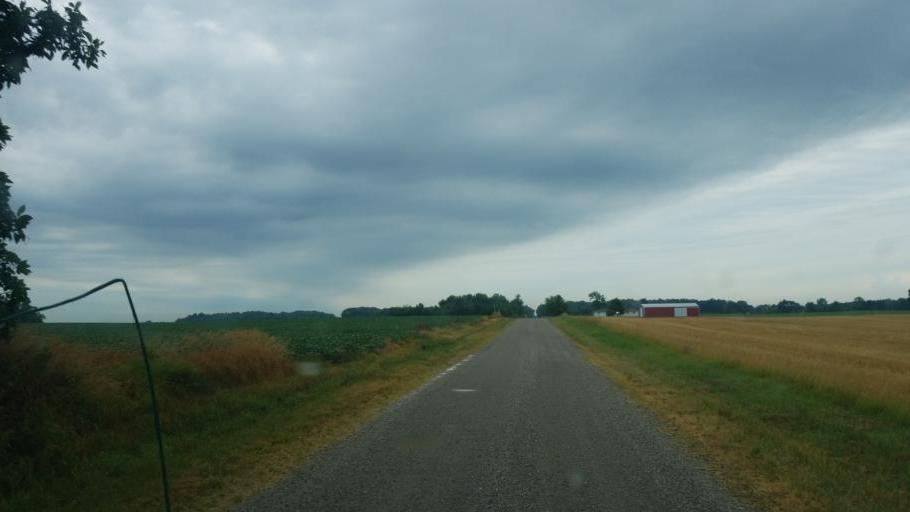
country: US
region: Indiana
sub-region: Steuben County
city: Hamilton
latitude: 41.4898
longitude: -84.9109
